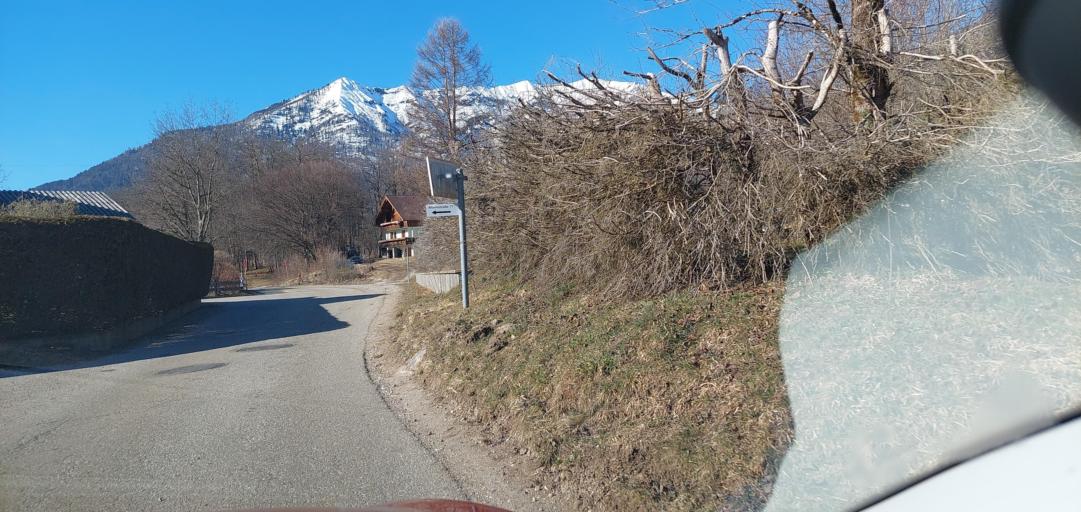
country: AT
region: Upper Austria
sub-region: Politischer Bezirk Gmunden
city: Bad Ischl
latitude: 47.7137
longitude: 13.5982
